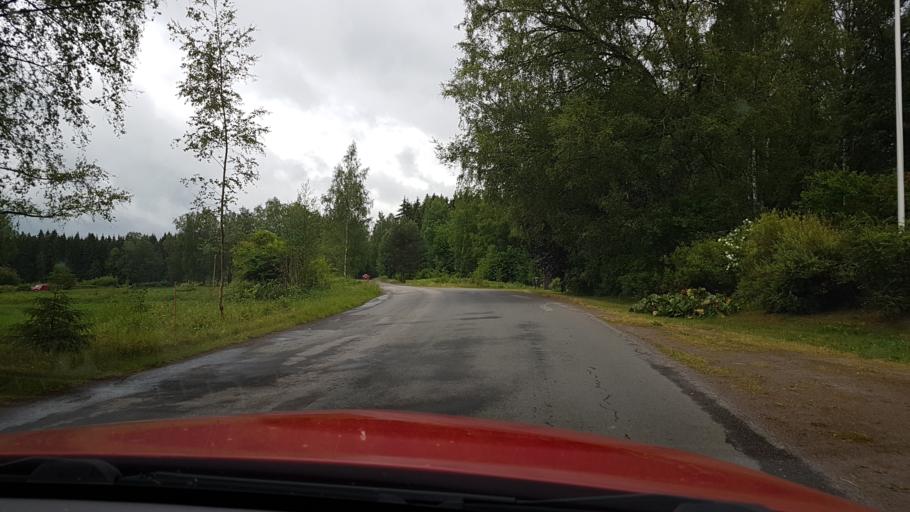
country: SE
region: Vaestra Goetaland
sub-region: Tibro Kommun
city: Tibro
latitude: 58.4289
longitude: 14.1293
